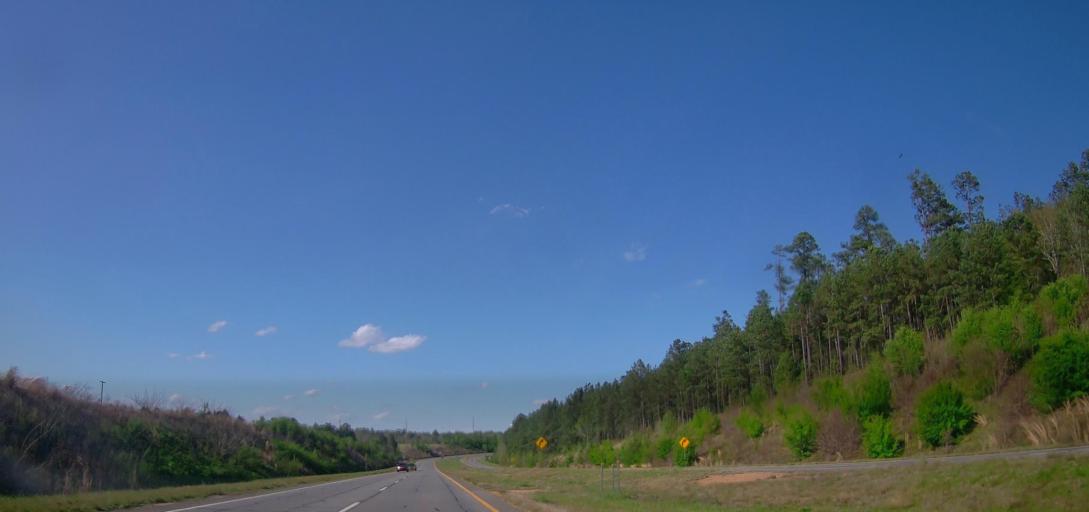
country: US
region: Georgia
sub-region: Baldwin County
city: Milledgeville
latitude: 33.0906
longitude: -83.2616
